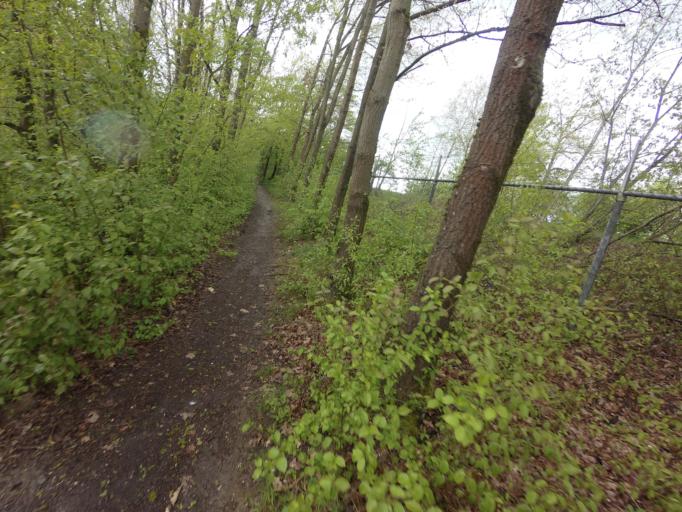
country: NL
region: Limburg
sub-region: Gemeente Kerkrade
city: Kerkrade
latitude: 50.8813
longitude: 6.0268
